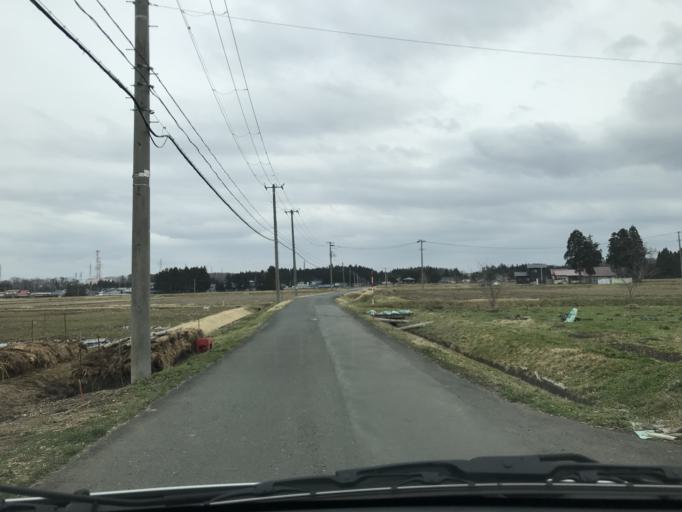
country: JP
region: Iwate
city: Kitakami
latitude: 39.2256
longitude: 141.0770
